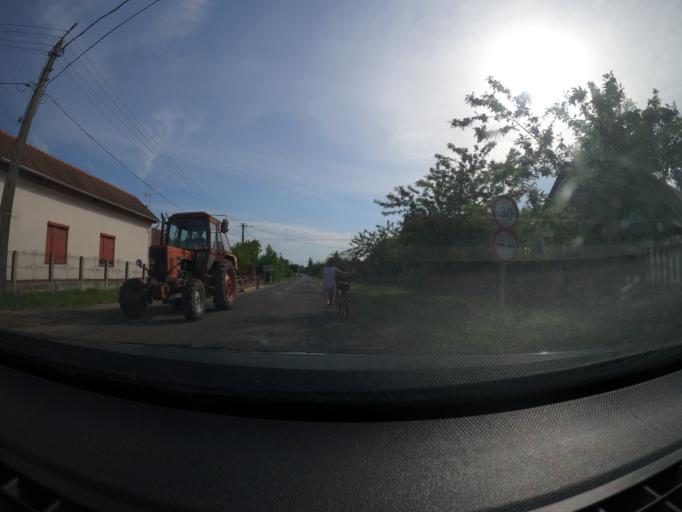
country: HU
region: Hajdu-Bihar
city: Nyirabrany
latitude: 47.5444
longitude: 22.0143
